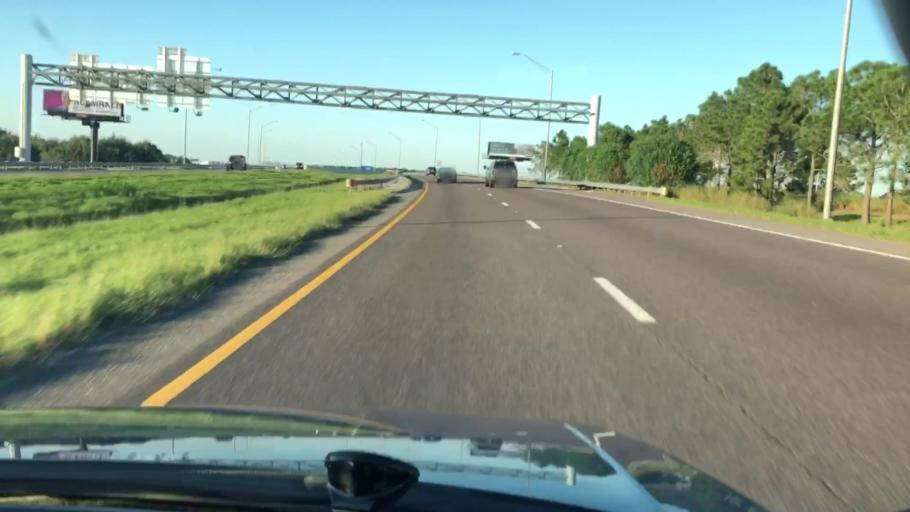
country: US
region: Florida
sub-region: Orange County
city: Ocoee
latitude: 28.5680
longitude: -81.5569
